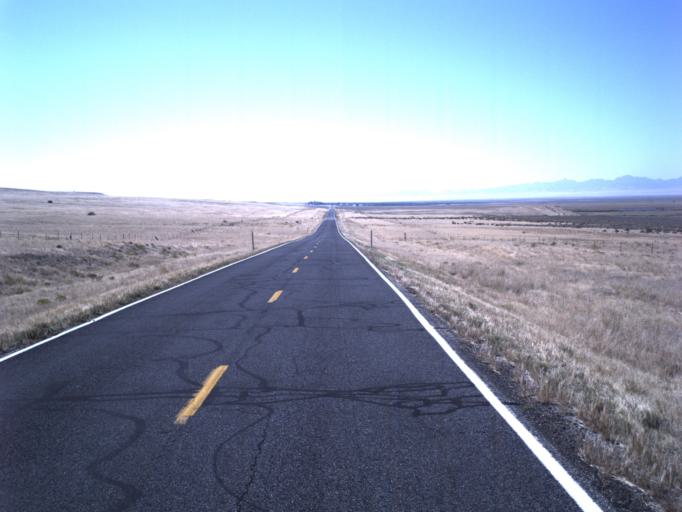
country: US
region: Utah
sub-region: Tooele County
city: Grantsville
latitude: 40.5758
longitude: -112.7279
